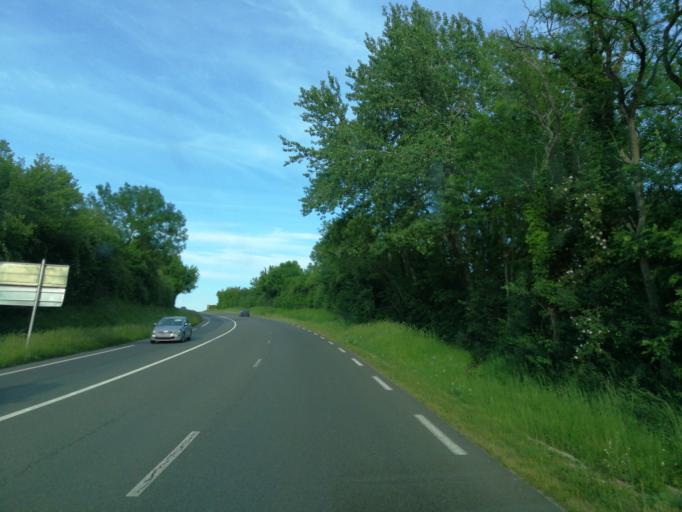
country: FR
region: Centre
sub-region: Departement d'Eure-et-Loir
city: Gallardon
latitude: 48.5014
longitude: 1.7270
